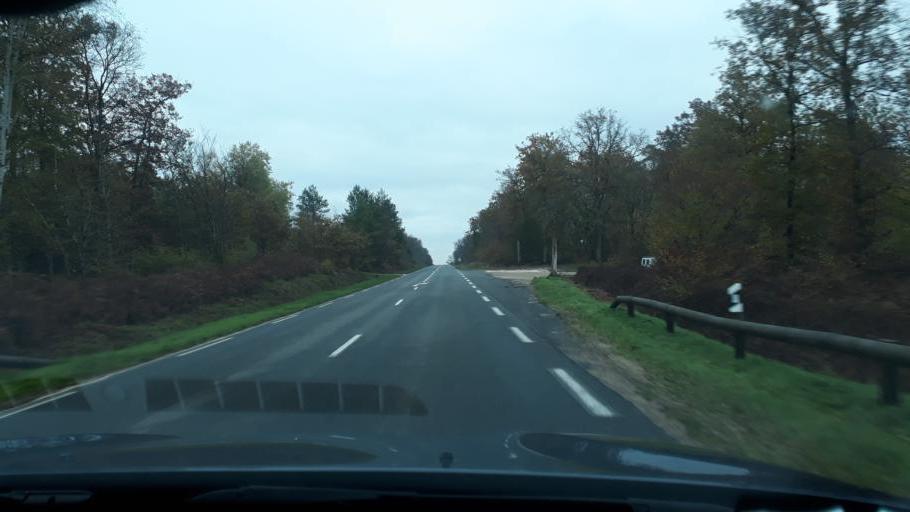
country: FR
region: Centre
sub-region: Departement du Loiret
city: Bouzy-la-Foret
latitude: 47.8310
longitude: 2.4222
